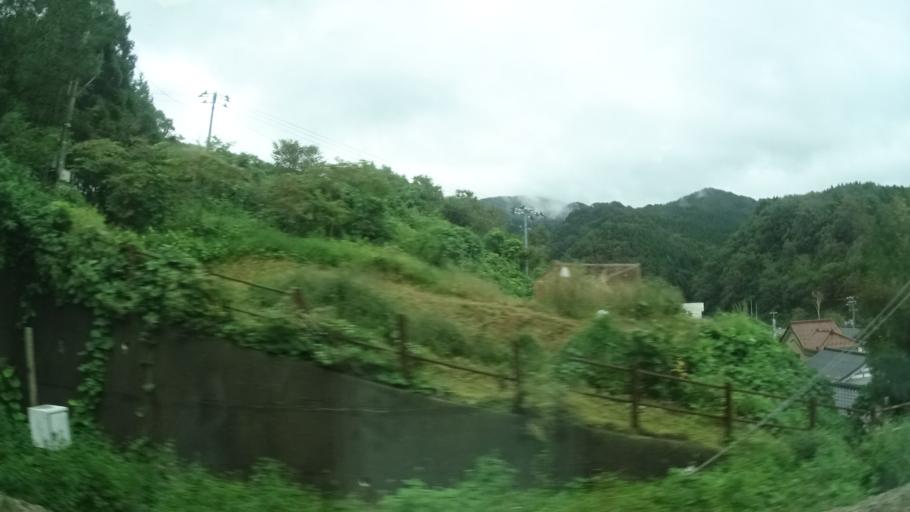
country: JP
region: Yamagata
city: Tsuruoka
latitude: 38.6845
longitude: 139.6391
